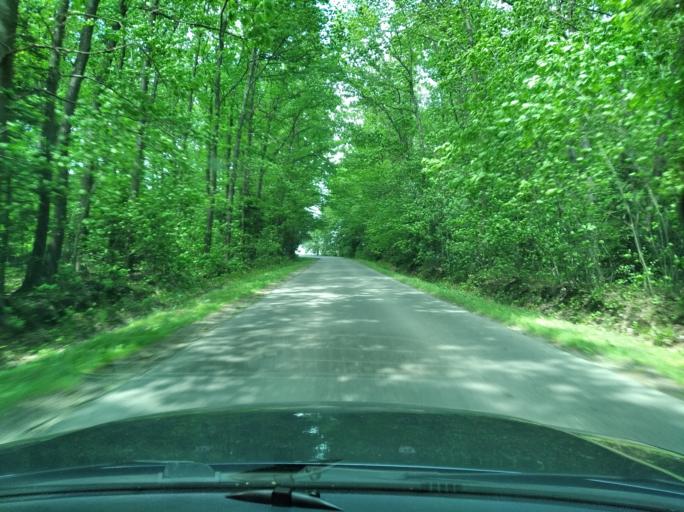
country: PL
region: Subcarpathian Voivodeship
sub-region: Powiat ropczycko-sedziszowski
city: Ropczyce
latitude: 50.0194
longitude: 21.6082
